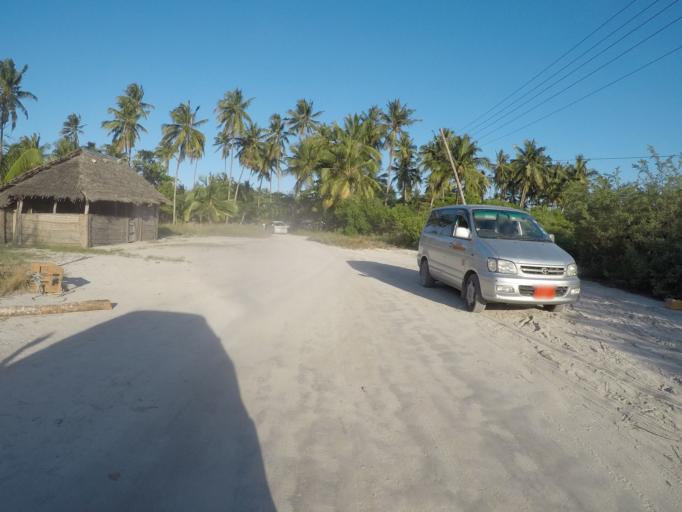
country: TZ
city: Kiwengwa
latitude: -6.1443
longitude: 39.4942
